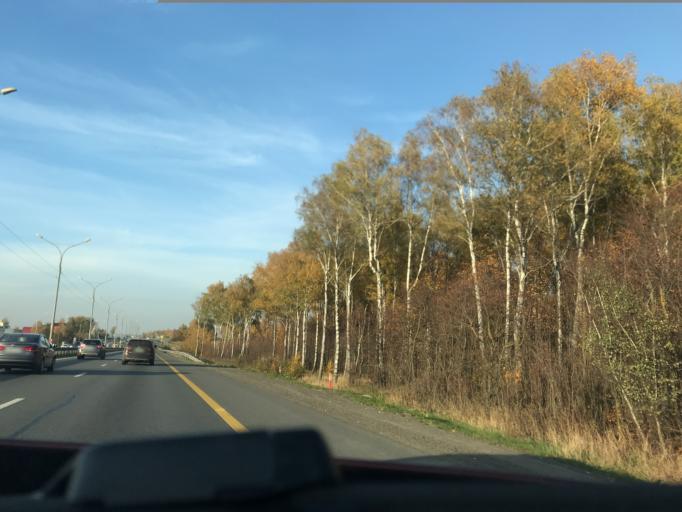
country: RU
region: Moskovskaya
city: Vostryakovo
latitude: 55.4662
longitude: 37.8540
